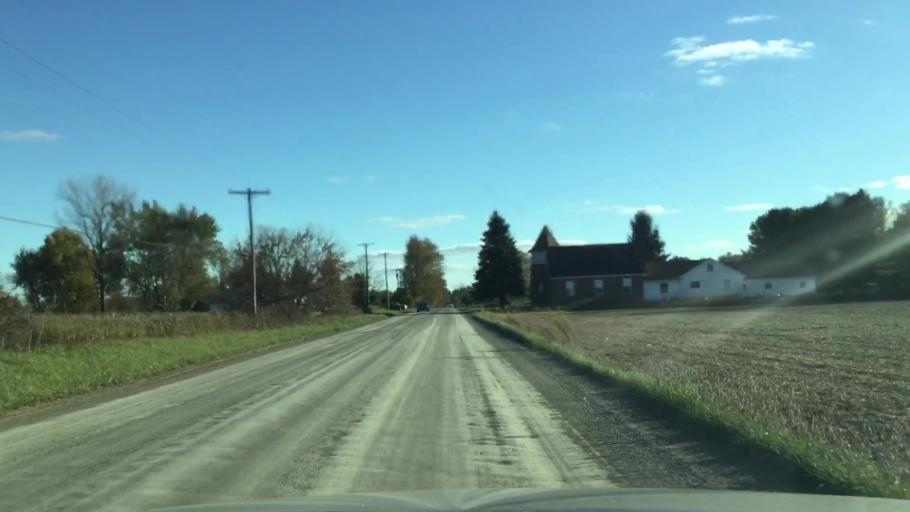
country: US
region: Michigan
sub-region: Lapeer County
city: Lapeer
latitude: 43.0691
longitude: -83.2272
